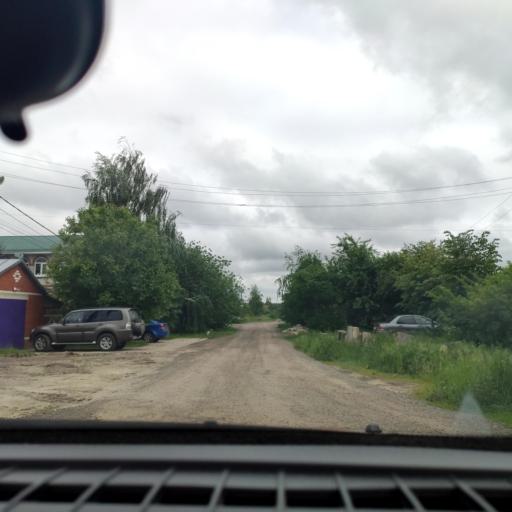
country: RU
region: Voronezj
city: Somovo
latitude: 51.6821
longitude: 39.3217
